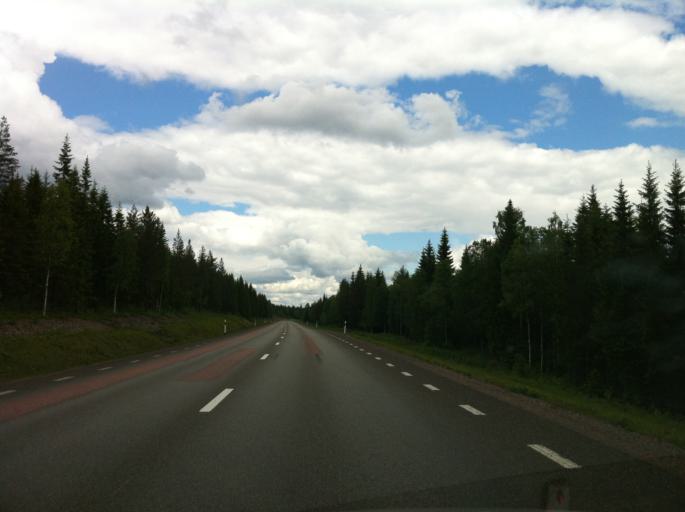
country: SE
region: Dalarna
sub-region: Malung-Saelens kommun
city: Malung
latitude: 60.6292
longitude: 13.6139
